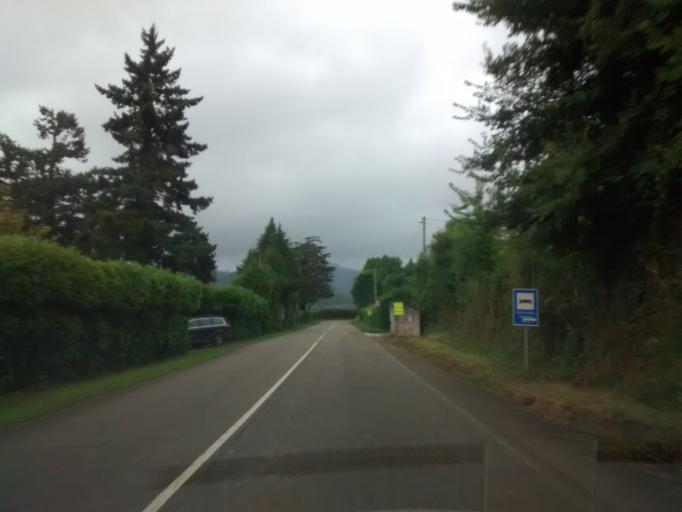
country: ES
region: Asturias
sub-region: Province of Asturias
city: Villaviciosa
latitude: 43.5174
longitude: -5.4061
